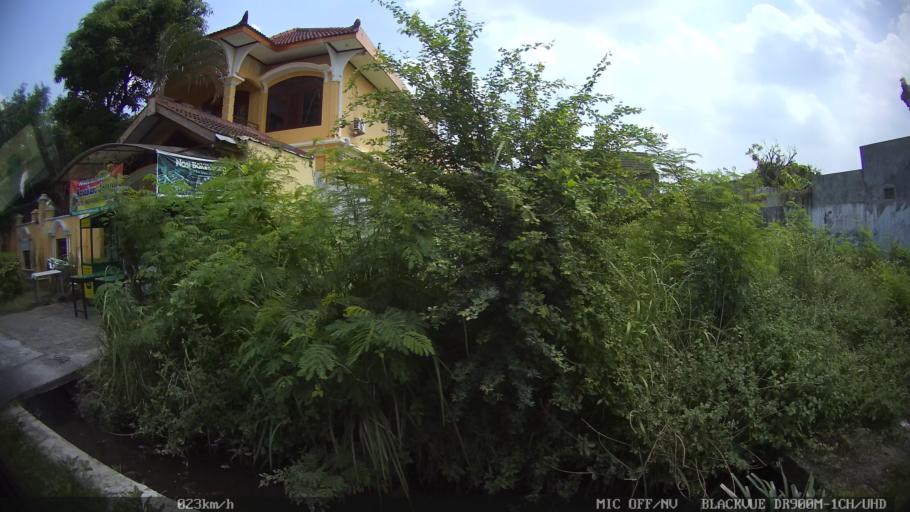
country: ID
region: Daerah Istimewa Yogyakarta
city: Yogyakarta
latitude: -7.8141
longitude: 110.3986
